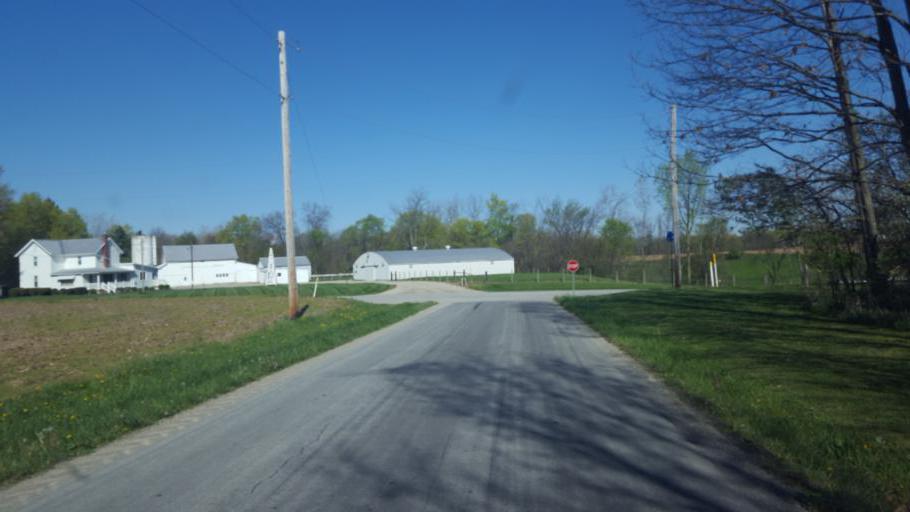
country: US
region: Ohio
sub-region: Wyandot County
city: Upper Sandusky
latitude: 40.9016
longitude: -83.2252
